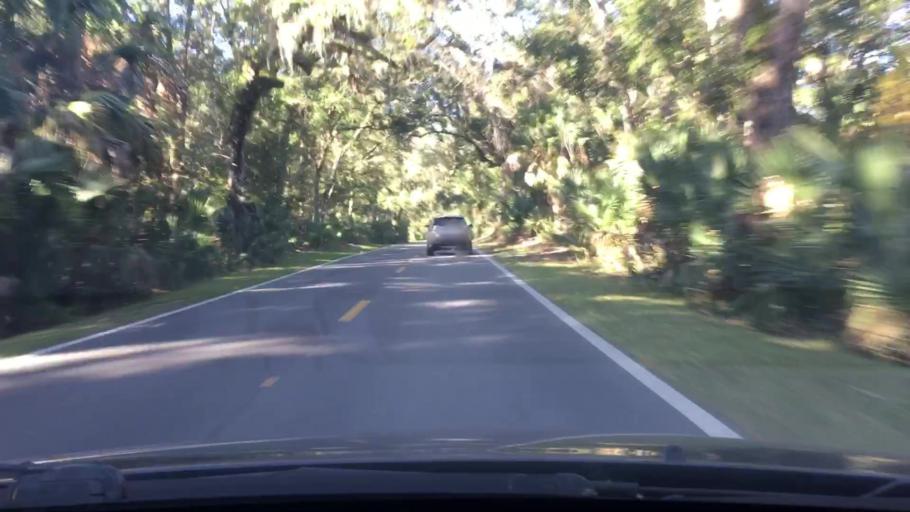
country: US
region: Florida
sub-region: Volusia County
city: Ormond-by-the-Sea
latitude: 29.3735
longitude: -81.1276
